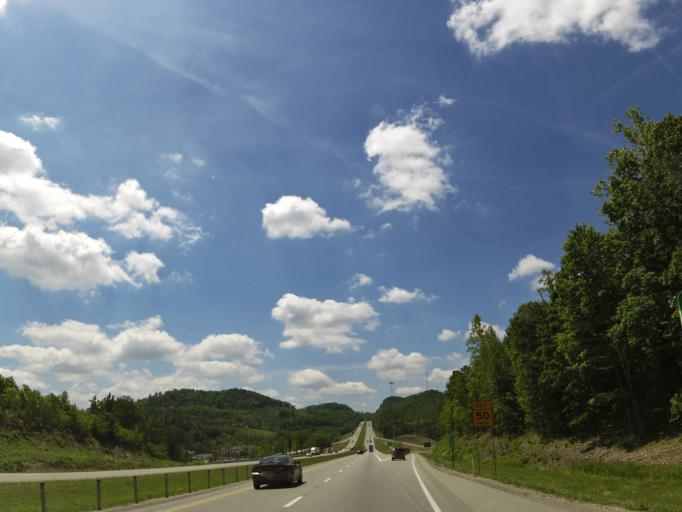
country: US
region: Kentucky
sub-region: Whitley County
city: Corbin
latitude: 36.9233
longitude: -84.1284
